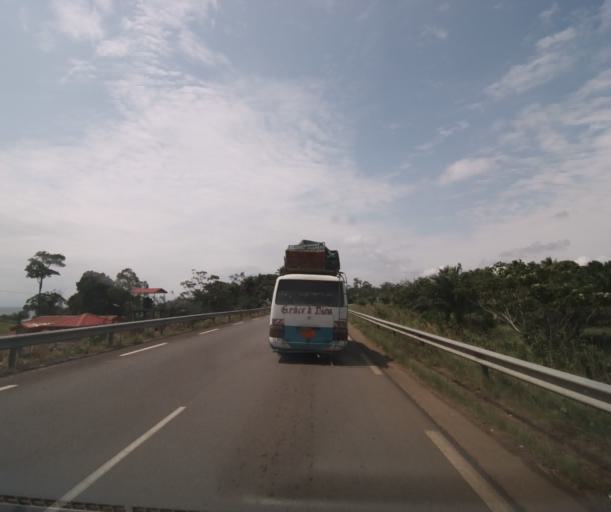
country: CM
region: South Province
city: Kribi
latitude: 3.0019
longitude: 9.9407
